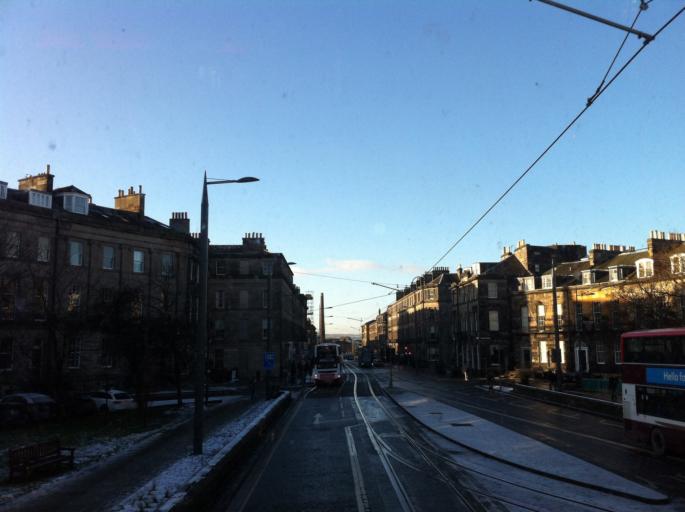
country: GB
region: Scotland
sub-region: Edinburgh
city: Edinburgh
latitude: 55.9482
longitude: -3.2124
